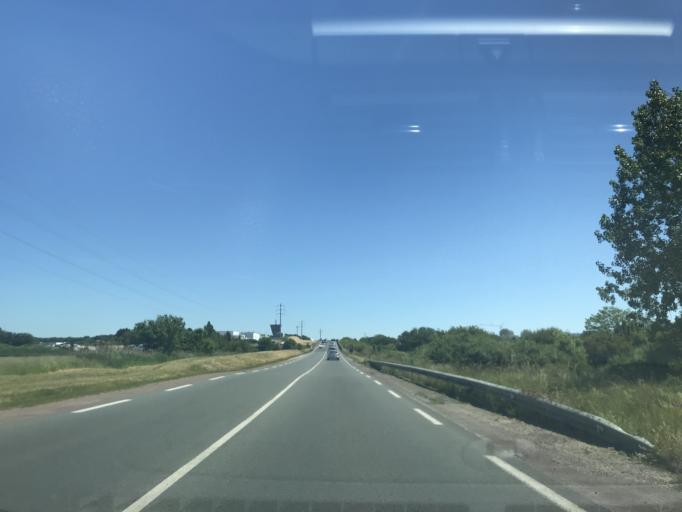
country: FR
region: Poitou-Charentes
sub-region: Departement de la Charente-Maritime
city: Royan
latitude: 45.6324
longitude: -1.0097
